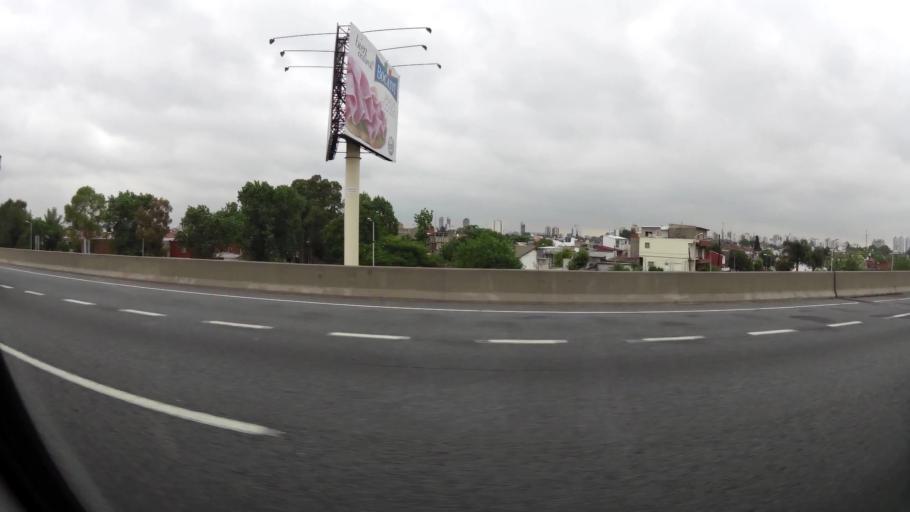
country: AR
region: Buenos Aires
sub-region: Partido de Avellaneda
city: Avellaneda
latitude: -34.6627
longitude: -58.3462
